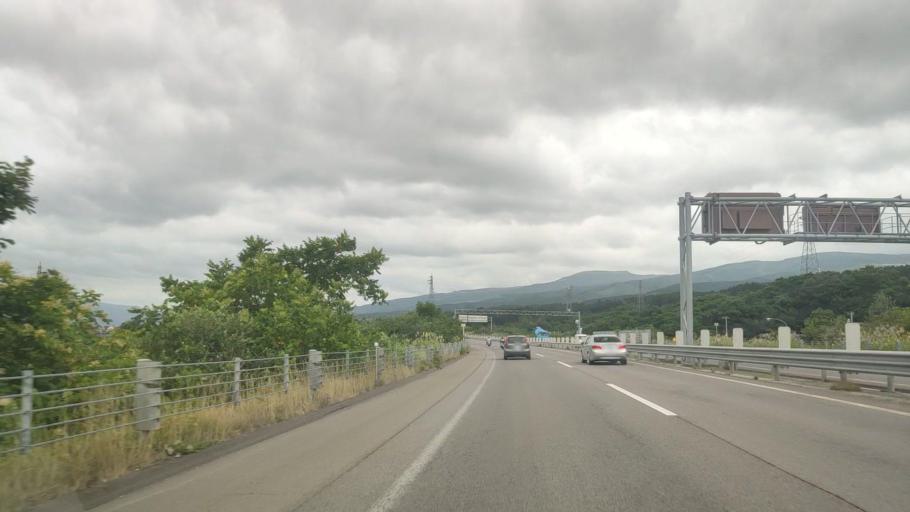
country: JP
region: Hokkaido
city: Nanae
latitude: 41.8544
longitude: 140.7382
